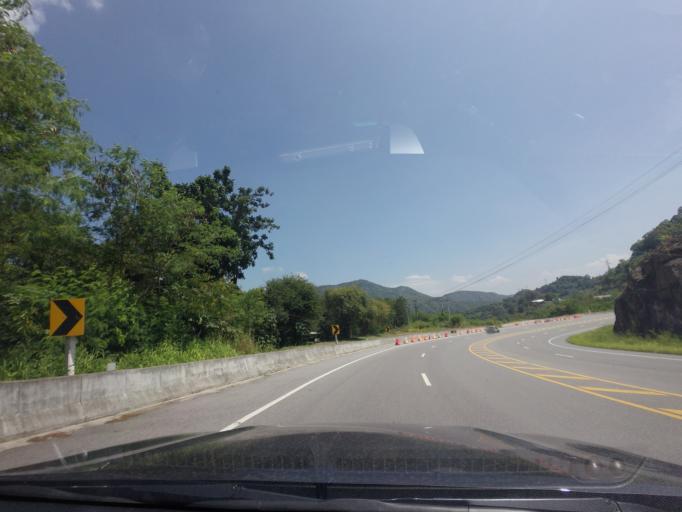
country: TH
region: Phetchabun
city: Lom Sak
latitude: 16.7814
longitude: 101.1036
